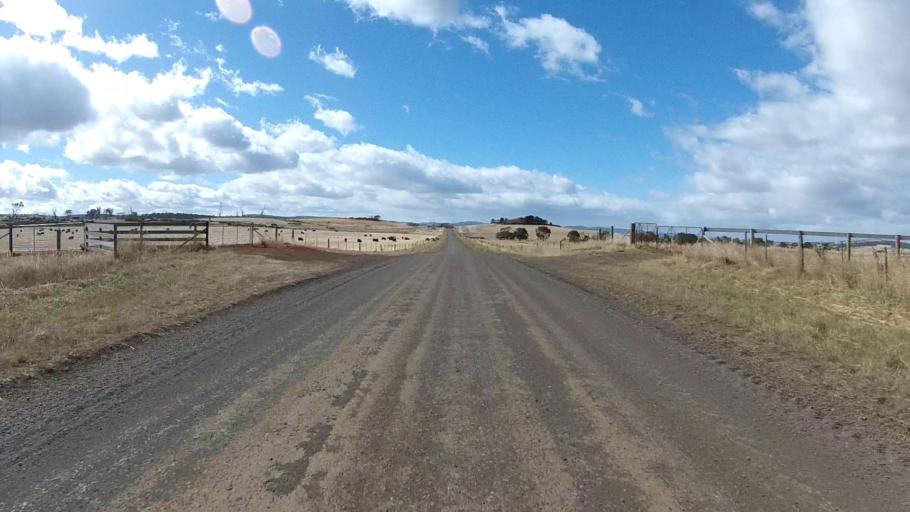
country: AU
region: Tasmania
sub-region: Northern Midlands
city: Evandale
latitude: -41.7123
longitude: 147.4122
